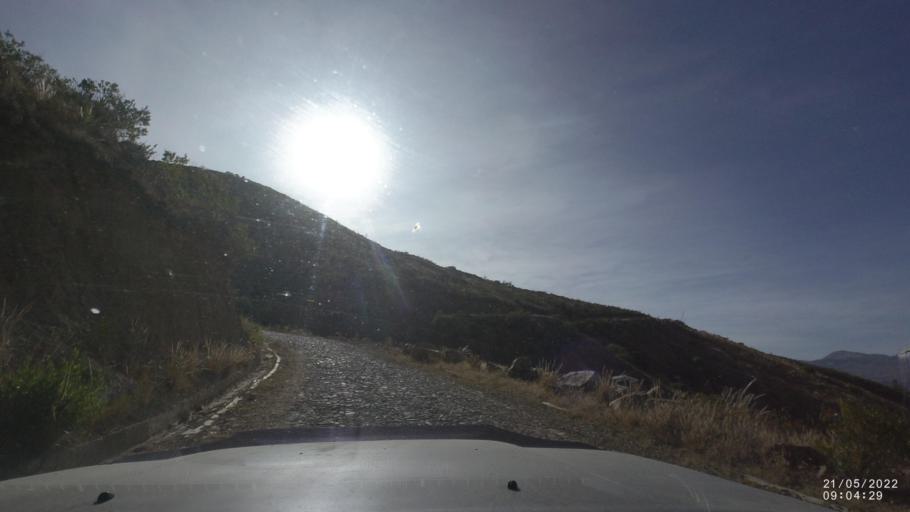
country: BO
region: Cochabamba
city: Cochabamba
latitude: -17.3795
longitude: -66.0263
